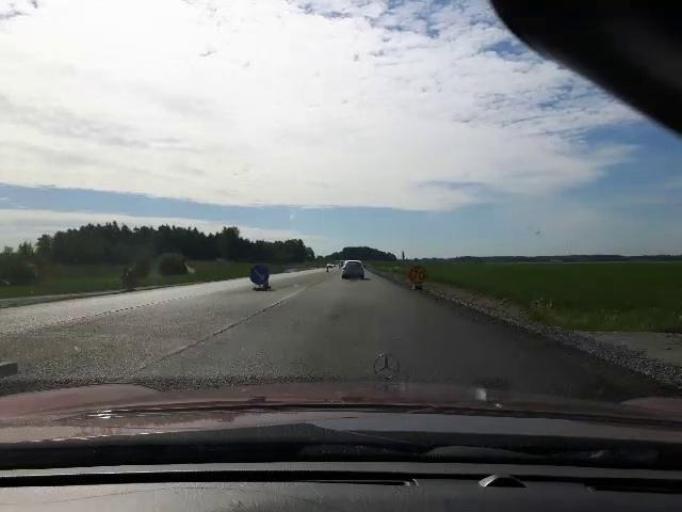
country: SE
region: Uppsala
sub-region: Enkopings Kommun
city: Irsta
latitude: 59.7624
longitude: 16.9199
